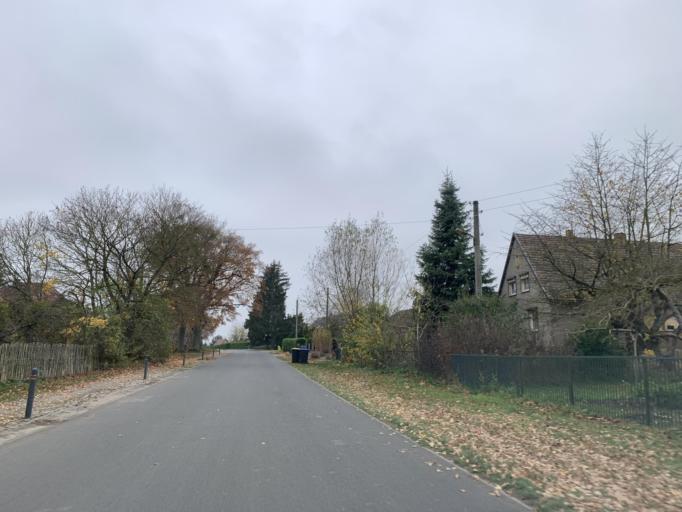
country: DE
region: Mecklenburg-Vorpommern
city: Blankensee
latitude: 53.3970
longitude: 13.2351
